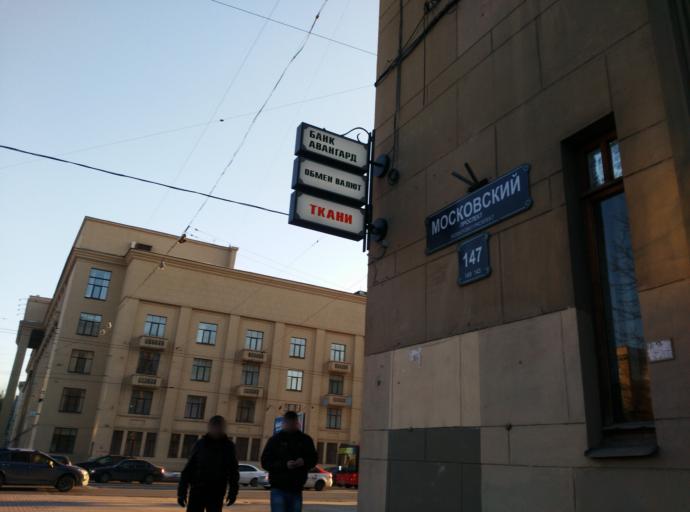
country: RU
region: St.-Petersburg
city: Kupchino
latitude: 59.8762
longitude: 30.3194
